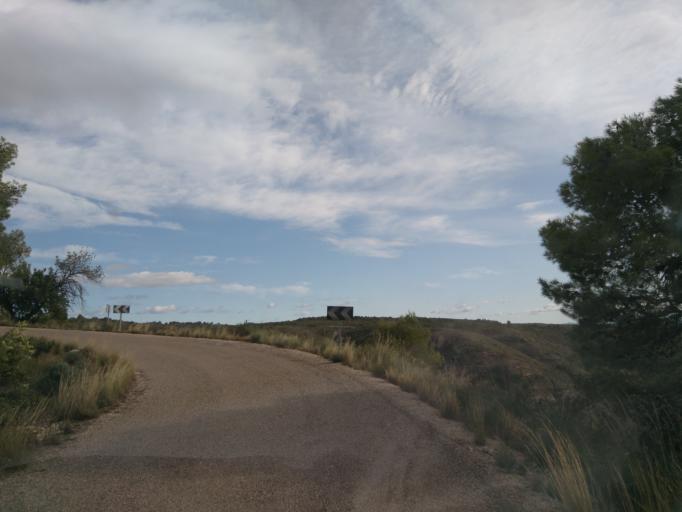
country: ES
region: Valencia
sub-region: Provincia de Valencia
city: Sumacarcer
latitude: 39.1459
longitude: -0.6434
